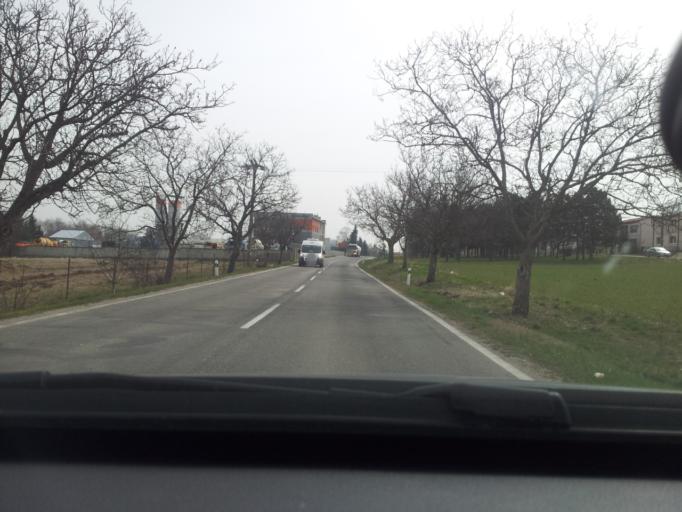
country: SK
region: Trnavsky
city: Hlohovec
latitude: 48.3730
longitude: 17.8865
